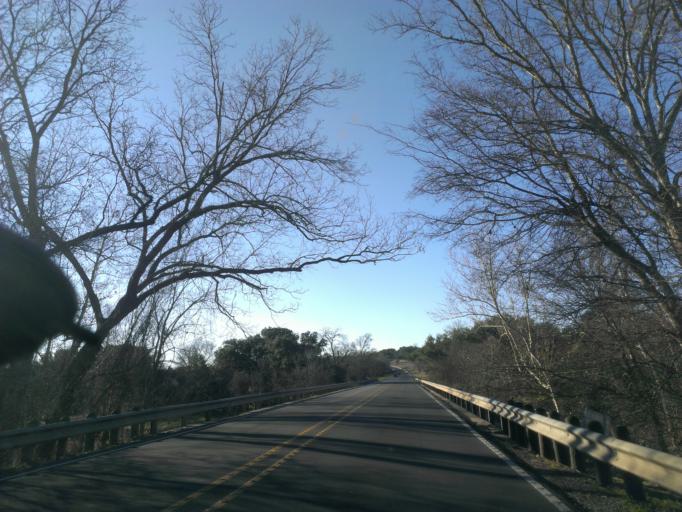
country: US
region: Texas
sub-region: Hays County
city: Dripping Springs
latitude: 30.1613
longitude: -98.0914
